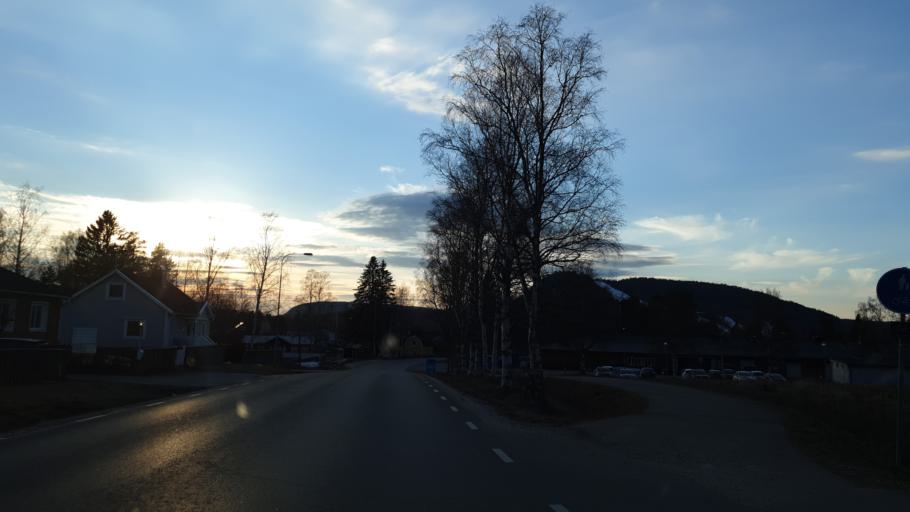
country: SE
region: Vaesternorrland
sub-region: Sundsvalls Kommun
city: Skottsund
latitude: 62.2890
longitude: 17.3915
